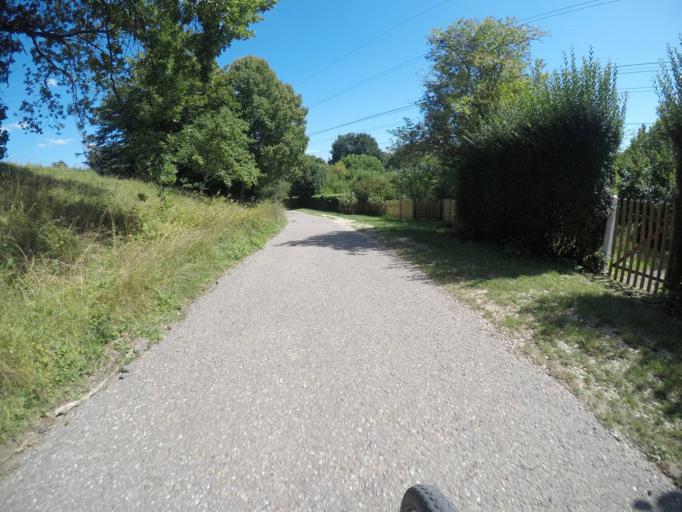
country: DE
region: Baden-Wuerttemberg
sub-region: Regierungsbezirk Stuttgart
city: Leinfelden-Echterdingen
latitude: 48.7048
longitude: 9.1947
